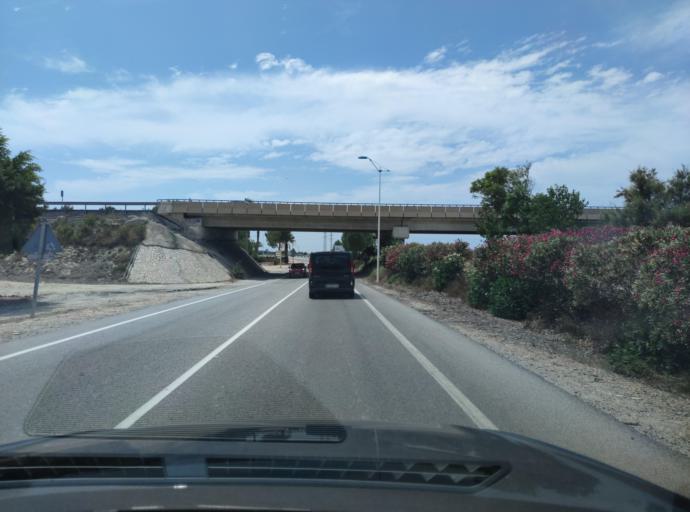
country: ES
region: Valencia
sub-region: Provincia de Alicante
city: Guardamar del Segura
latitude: 38.0963
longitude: -0.6641
